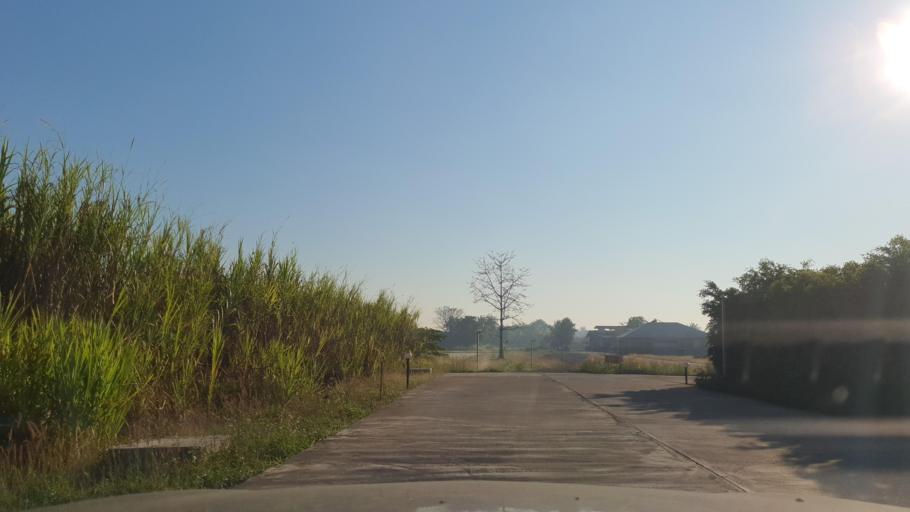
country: TH
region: Chiang Mai
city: Hang Dong
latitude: 18.6957
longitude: 98.9700
